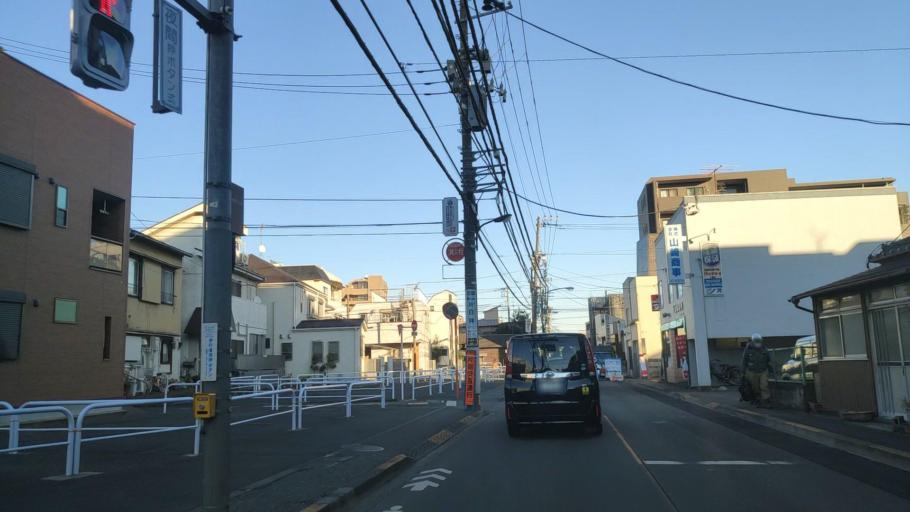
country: JP
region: Tokyo
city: Mitaka-shi
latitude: 35.6924
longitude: 139.5628
